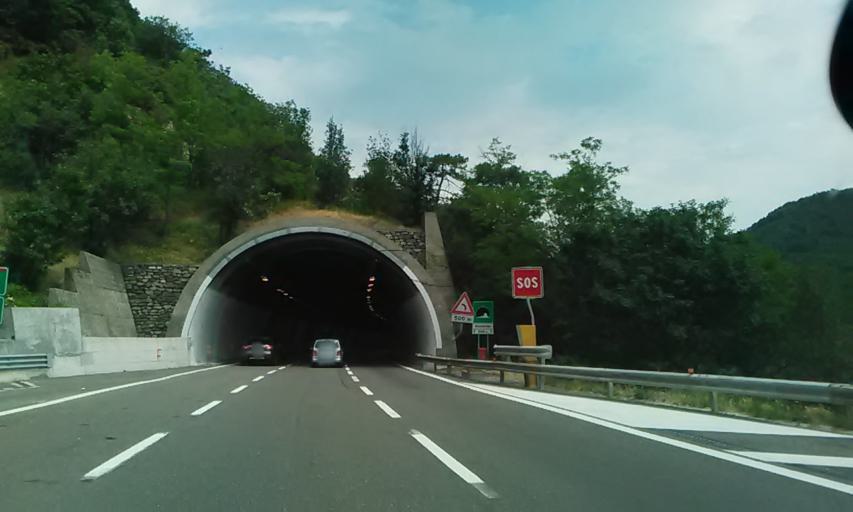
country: IT
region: Liguria
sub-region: Provincia di Genova
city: Rossiglione
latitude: 44.5791
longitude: 8.6598
